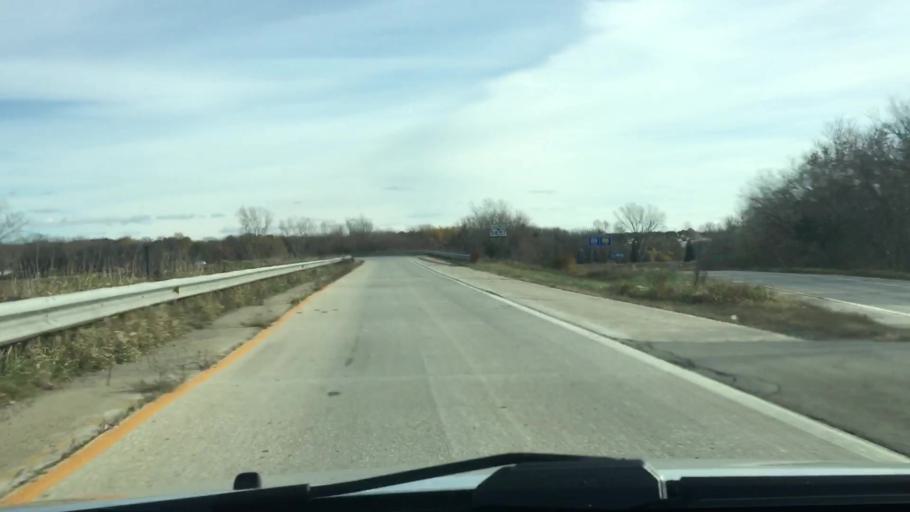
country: US
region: Wisconsin
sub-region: Brown County
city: Green Bay
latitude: 44.5178
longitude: -87.9604
